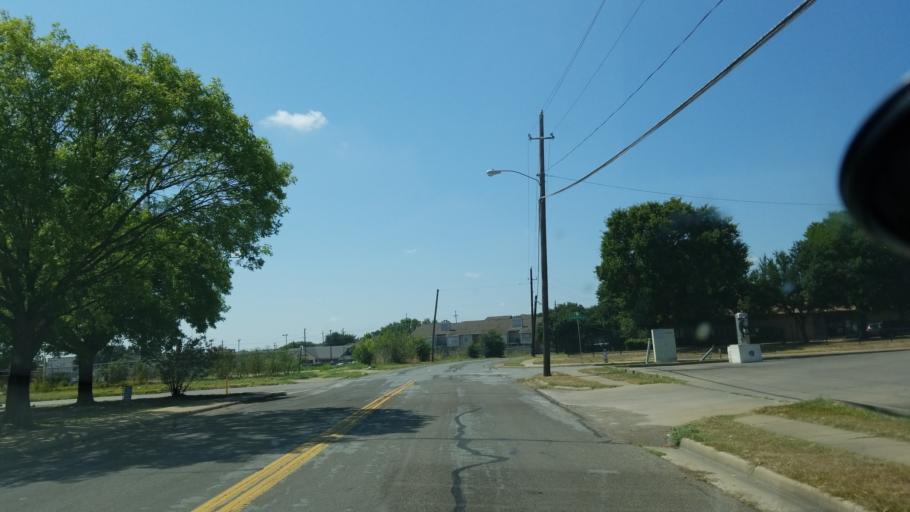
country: US
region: Texas
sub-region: Dallas County
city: Duncanville
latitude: 32.6611
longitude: -96.8841
